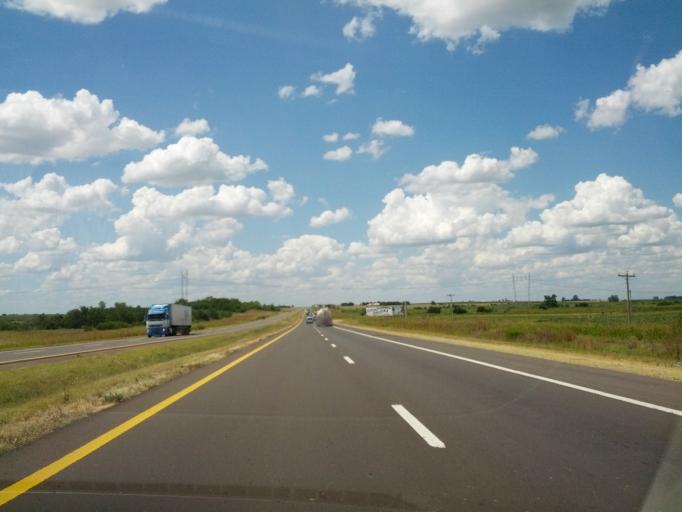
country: AR
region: Entre Rios
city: Colonia Elia
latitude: -32.5713
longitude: -58.3799
